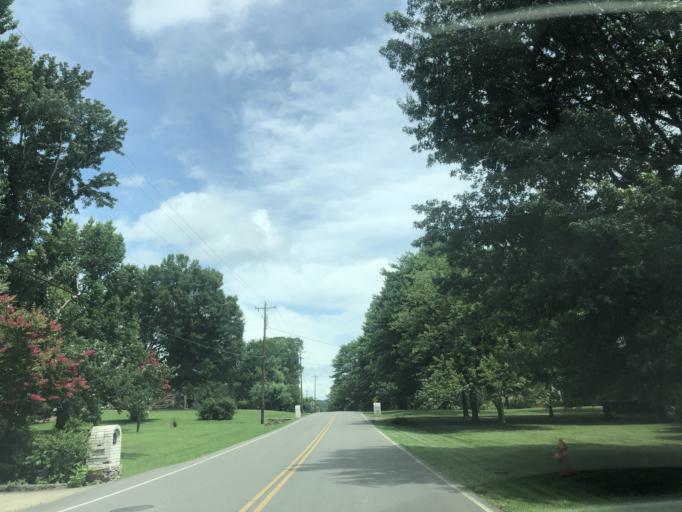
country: US
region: Tennessee
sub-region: Davidson County
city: Forest Hills
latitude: 36.0647
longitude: -86.8203
